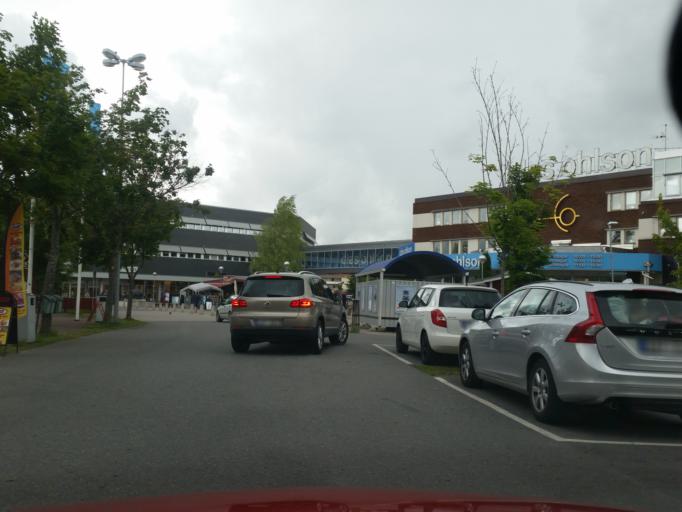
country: SE
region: Dalarna
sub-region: Leksand Municipality
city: Smedby
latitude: 60.6740
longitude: 15.0889
